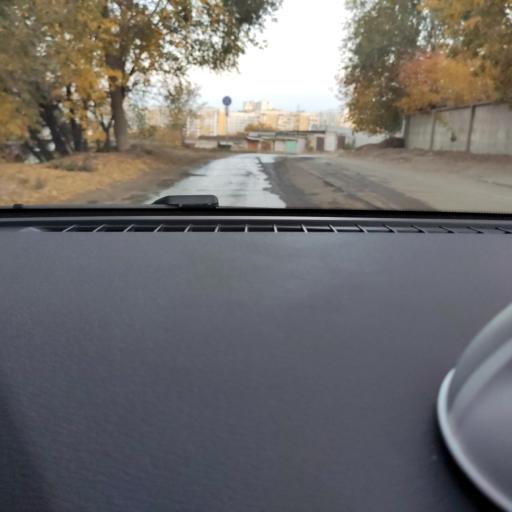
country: RU
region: Samara
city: Samara
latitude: 53.1831
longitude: 50.1439
